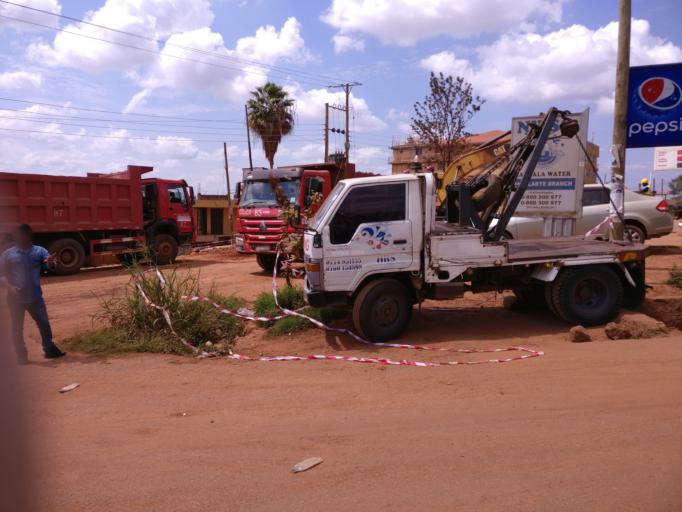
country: UG
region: Central Region
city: Kampala Central Division
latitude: 0.3203
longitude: 32.5632
